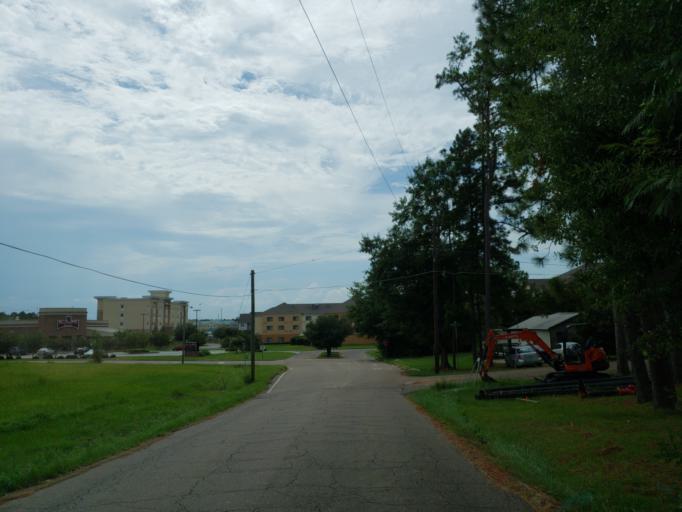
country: US
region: Mississippi
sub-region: Lamar County
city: Arnold Line
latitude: 31.3285
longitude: -89.3471
